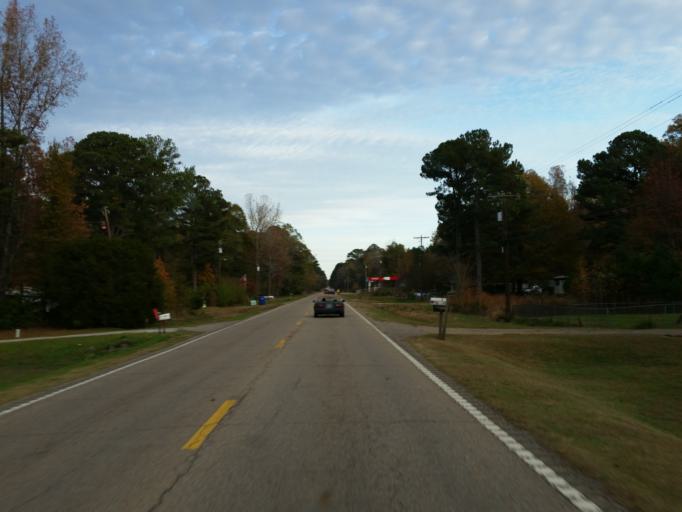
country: US
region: Mississippi
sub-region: Lauderdale County
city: Marion
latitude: 32.4195
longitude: -88.5268
